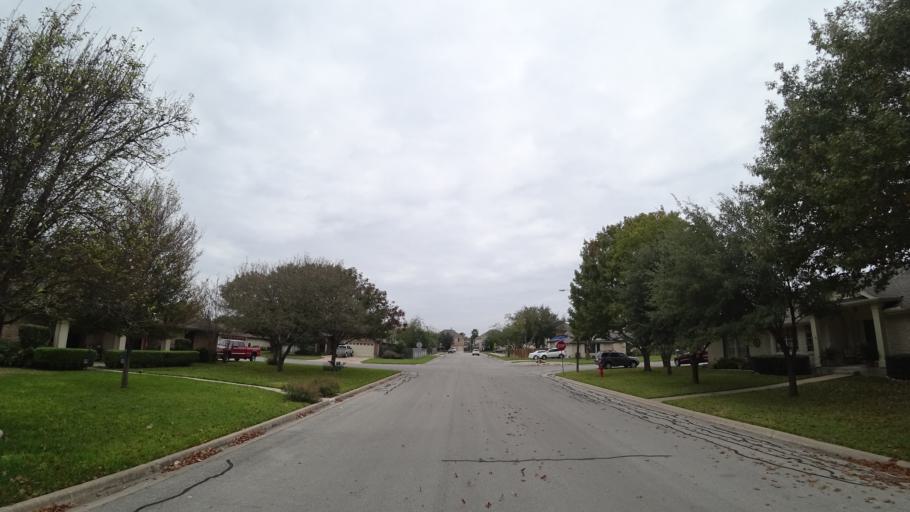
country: US
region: Texas
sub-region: Travis County
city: Pflugerville
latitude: 30.4517
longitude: -97.6218
